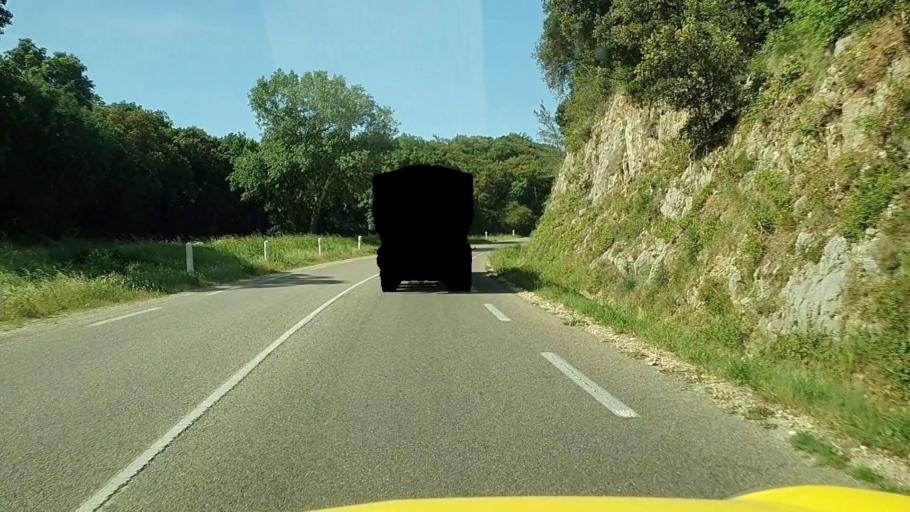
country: FR
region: Languedoc-Roussillon
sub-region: Departement du Gard
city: Connaux
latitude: 44.0636
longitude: 4.5753
